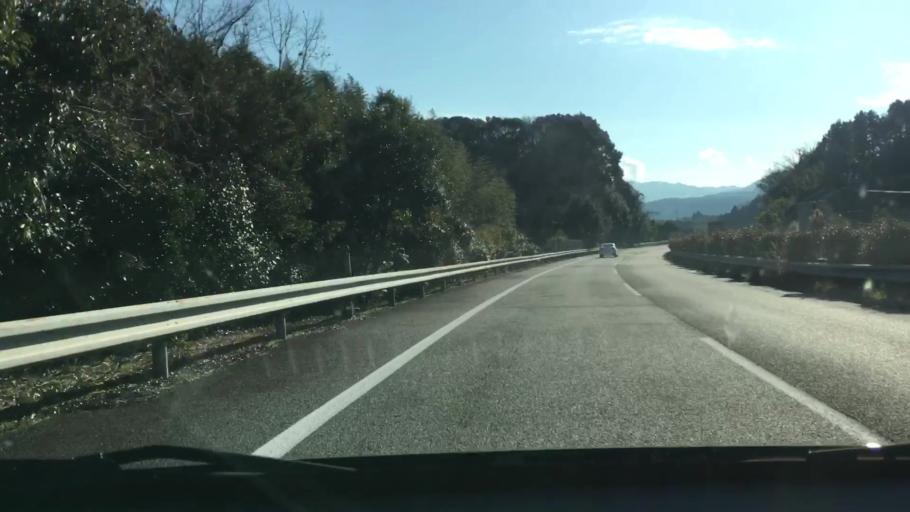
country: JP
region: Kumamoto
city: Hitoyoshi
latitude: 32.2174
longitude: 130.7799
